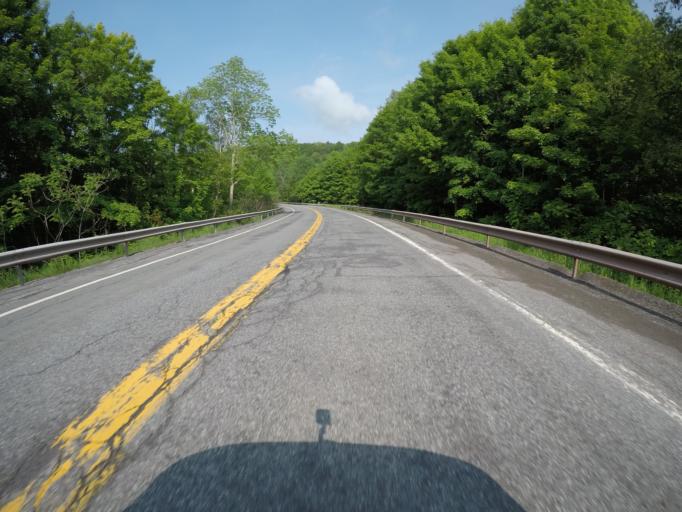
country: US
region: New York
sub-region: Delaware County
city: Delhi
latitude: 42.1213
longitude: -74.7387
